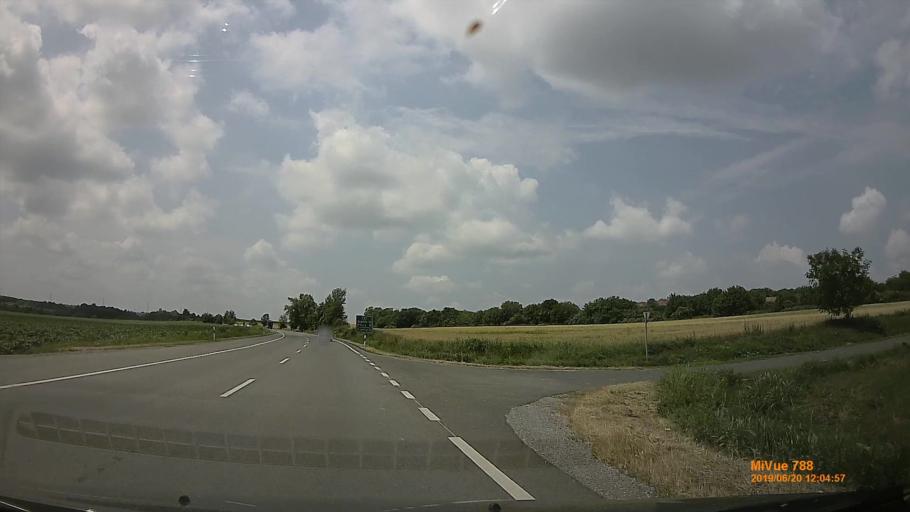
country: HU
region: Baranya
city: Pecsvarad
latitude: 46.1509
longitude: 18.4162
